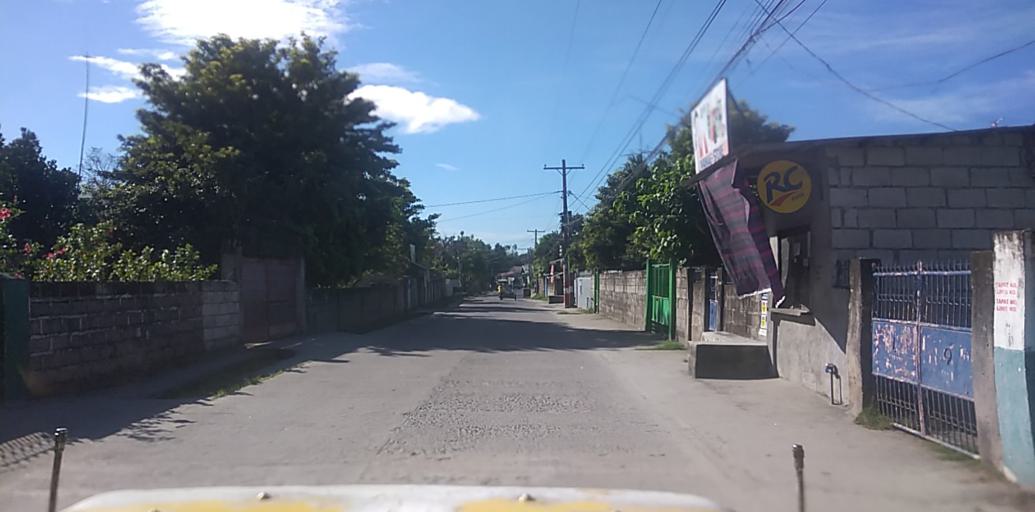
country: PH
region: Central Luzon
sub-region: Province of Pampanga
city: San Patricio
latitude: 15.1011
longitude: 120.7137
